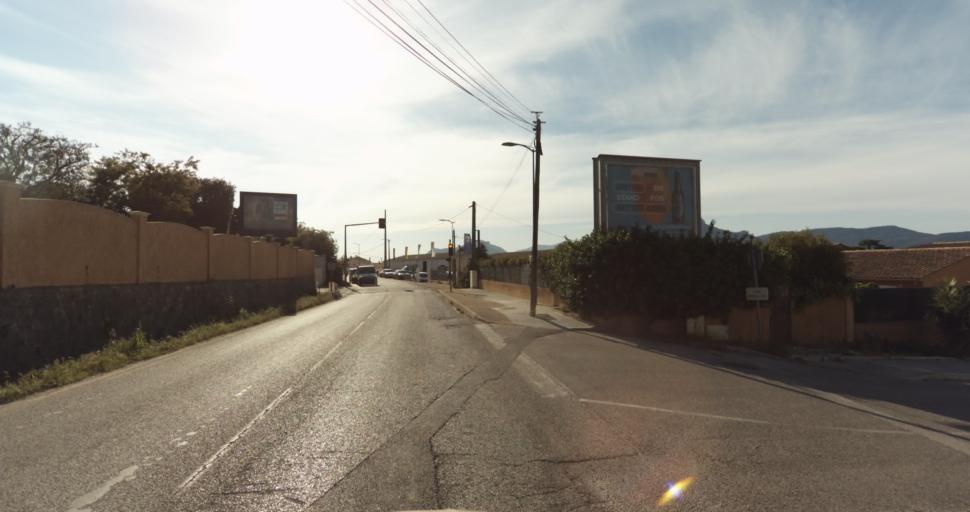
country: FR
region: Provence-Alpes-Cote d'Azur
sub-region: Departement du Var
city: Carqueiranne
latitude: 43.1192
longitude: 6.0666
